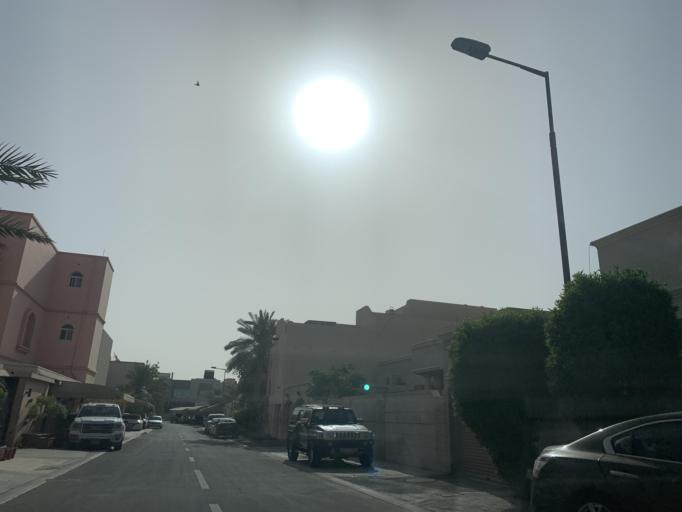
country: BH
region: Northern
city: Ar Rifa'
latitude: 26.1447
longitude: 50.5826
